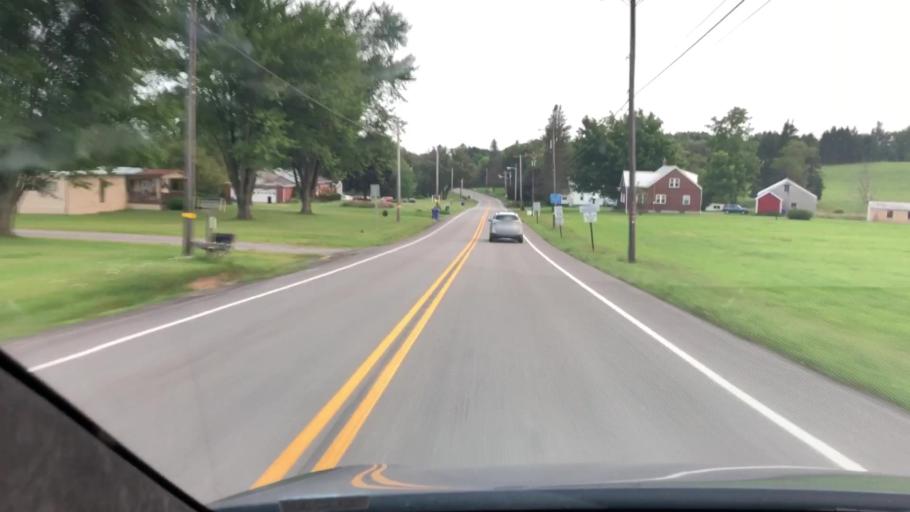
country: US
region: Pennsylvania
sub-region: Mercer County
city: Grove City
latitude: 41.1456
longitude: -80.0082
